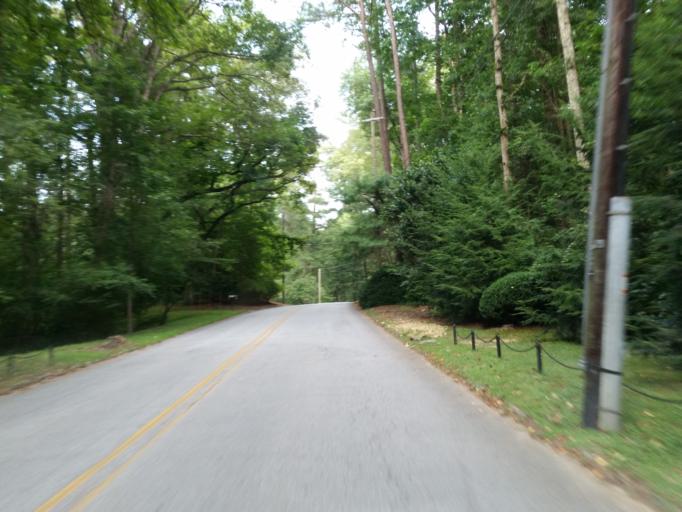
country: US
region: Georgia
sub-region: Cobb County
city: Vinings
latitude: 33.8450
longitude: -84.4412
